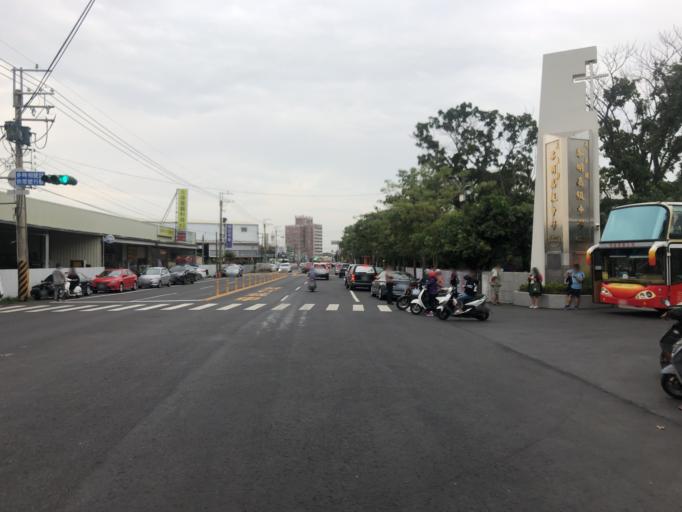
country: TW
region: Taiwan
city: Xinying
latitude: 23.1730
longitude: 120.2461
